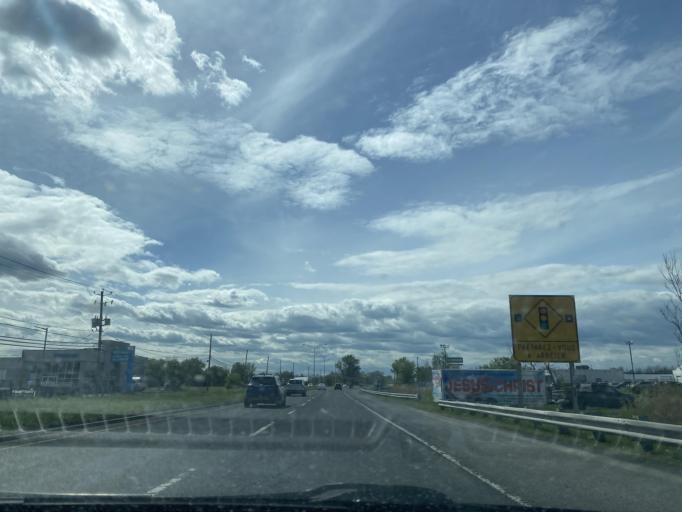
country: CA
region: Quebec
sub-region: Monteregie
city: Carignan
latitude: 45.4618
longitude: -73.3282
